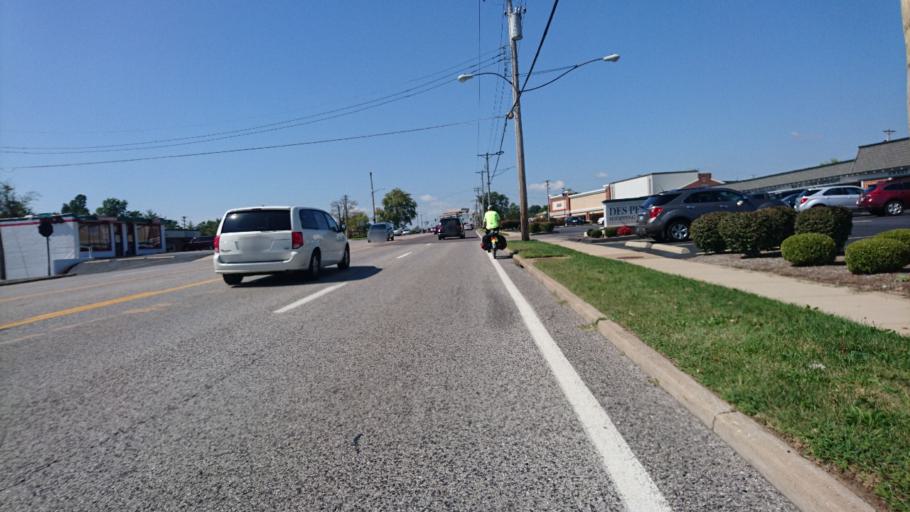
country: US
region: Missouri
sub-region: Saint Louis County
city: Des Peres
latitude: 38.6021
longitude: -90.4360
